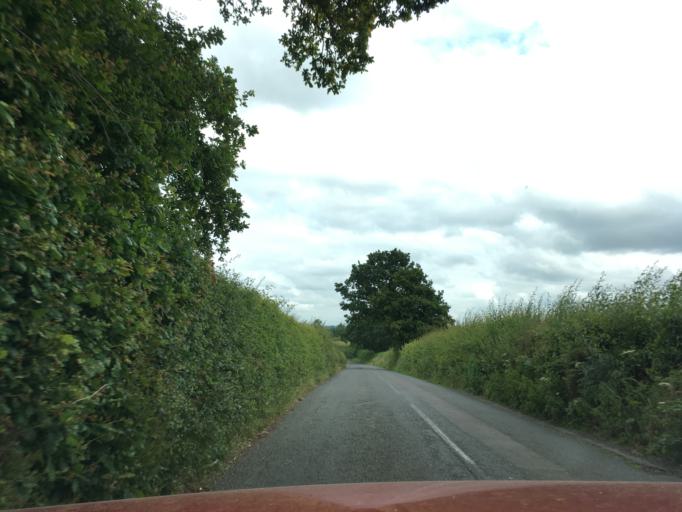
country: GB
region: England
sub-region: Oxfordshire
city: Shipton under Wychwood
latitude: 51.8895
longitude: -1.6435
